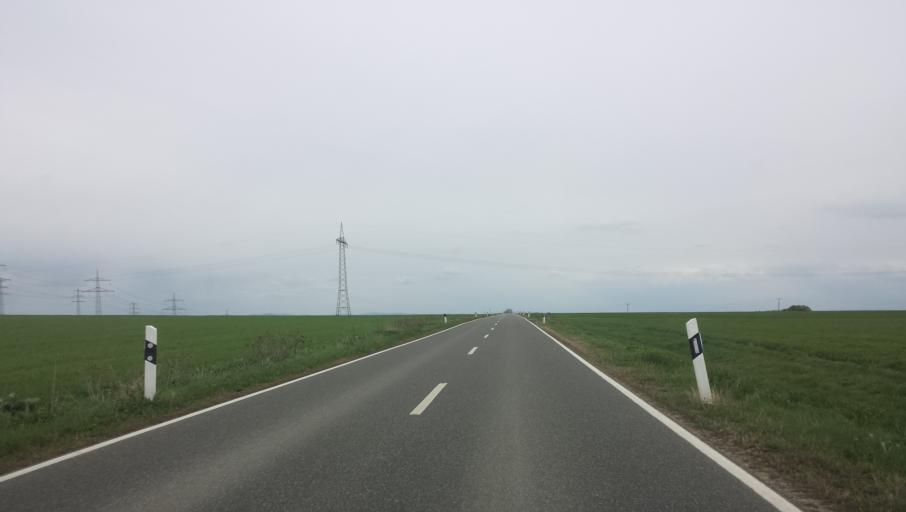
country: DE
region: Rheinland-Pfalz
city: Hochborn
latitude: 49.7245
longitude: 8.2076
